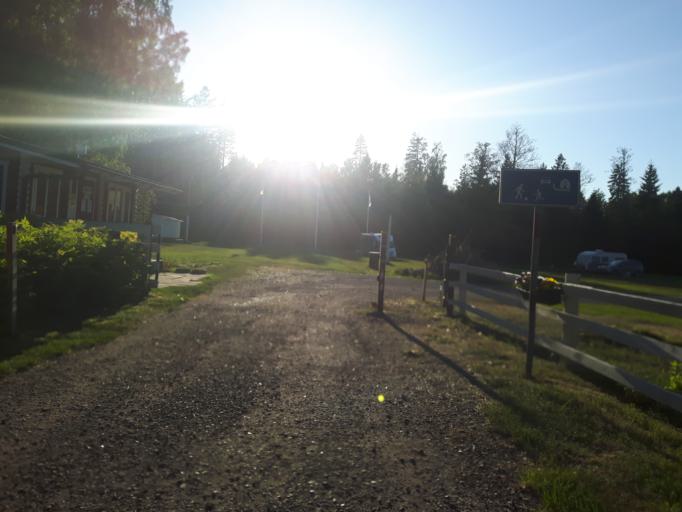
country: EE
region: Harju
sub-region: Loksa linn
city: Loksa
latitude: 59.5759
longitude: 25.9362
